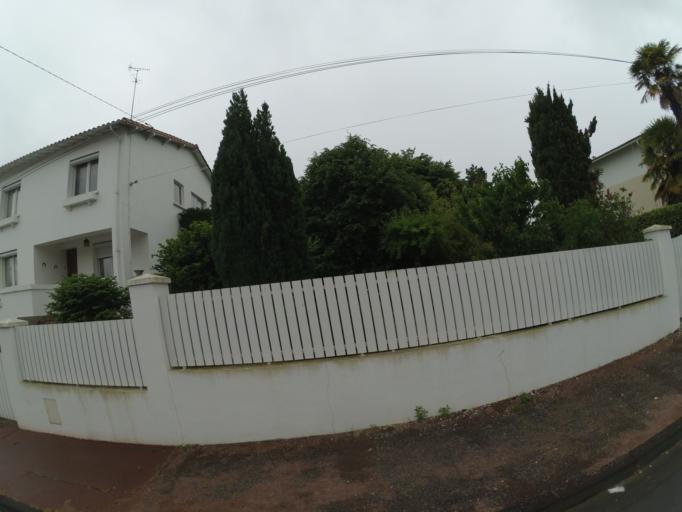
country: FR
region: Poitou-Charentes
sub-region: Departement de la Charente-Maritime
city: Saint-Georges-de-Didonne
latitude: 45.6201
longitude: -1.0077
